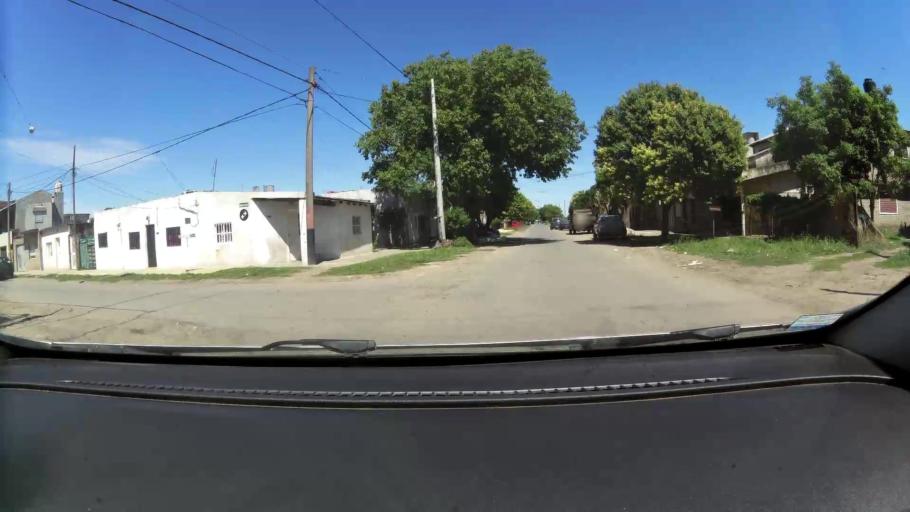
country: AR
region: Santa Fe
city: Perez
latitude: -32.9641
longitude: -60.7141
